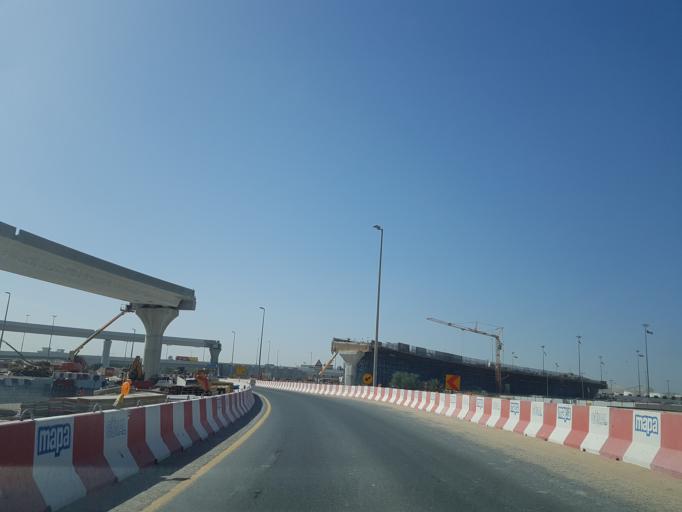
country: AE
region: Dubai
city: Dubai
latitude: 25.0153
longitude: 55.0932
